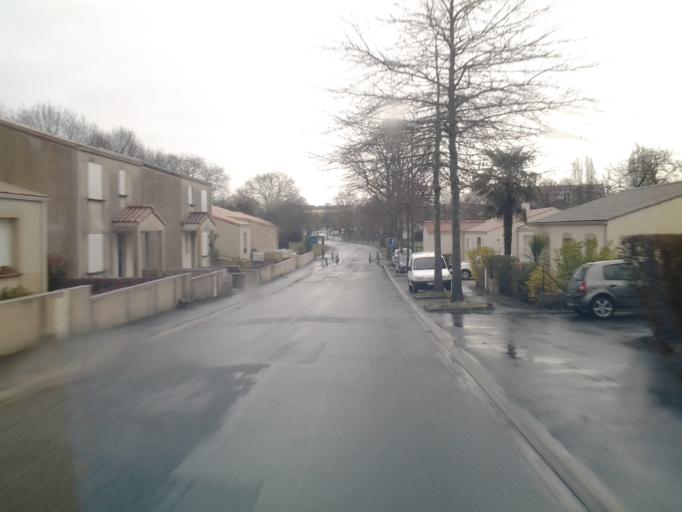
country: FR
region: Pays de la Loire
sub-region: Departement de la Vendee
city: La Roche-sur-Yon
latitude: 46.6769
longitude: -1.4462
